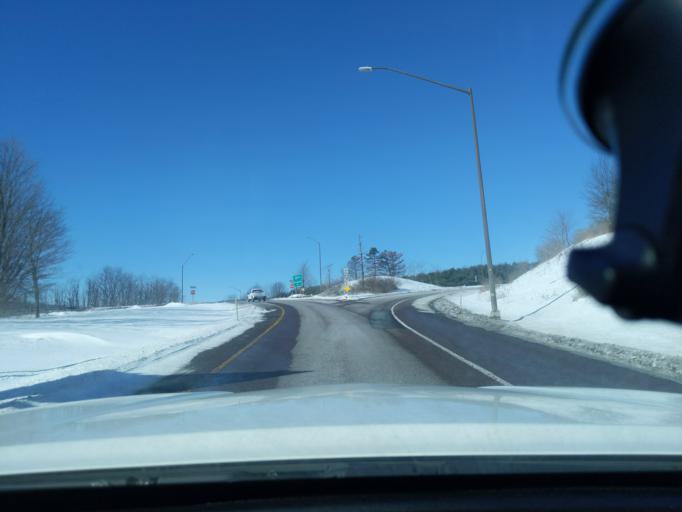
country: US
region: Maryland
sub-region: Allegany County
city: Frostburg
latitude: 39.6334
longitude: -78.9166
